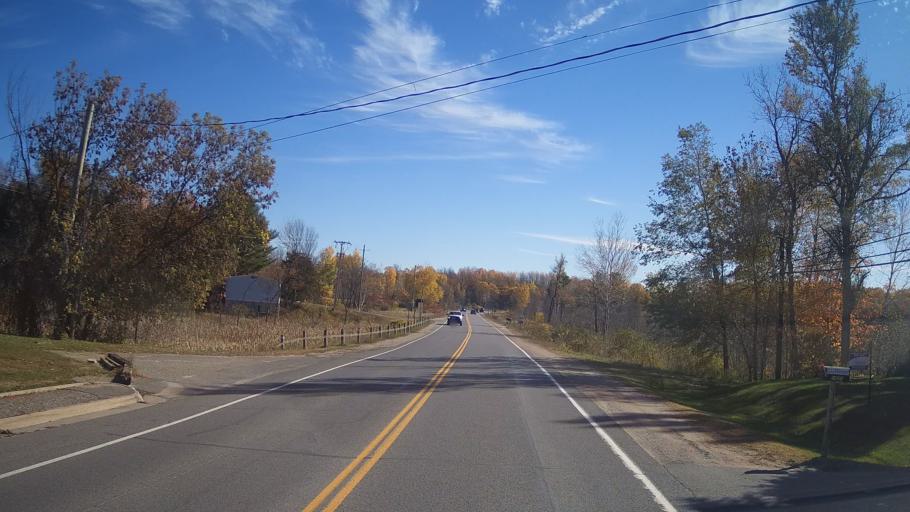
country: CA
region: Ontario
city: Perth
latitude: 44.7645
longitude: -76.6879
